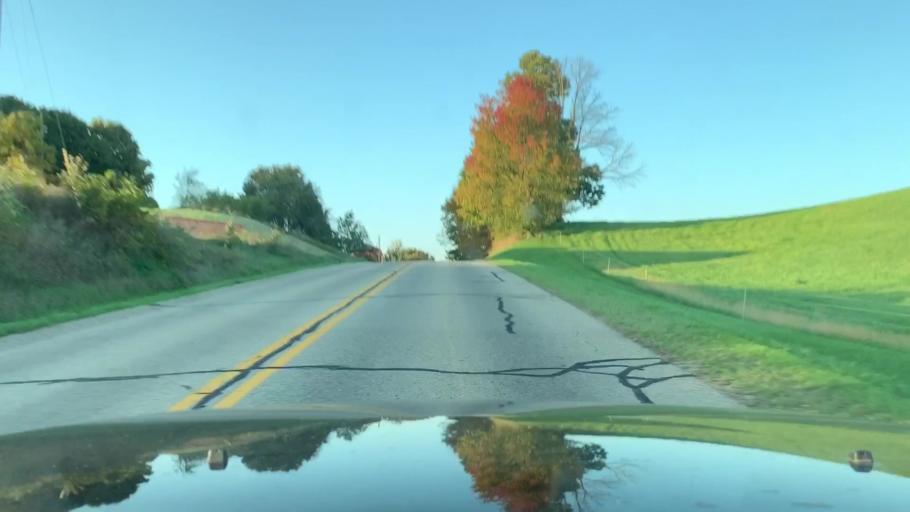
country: US
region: Michigan
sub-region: Kent County
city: Byron Center
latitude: 42.8145
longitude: -85.8026
